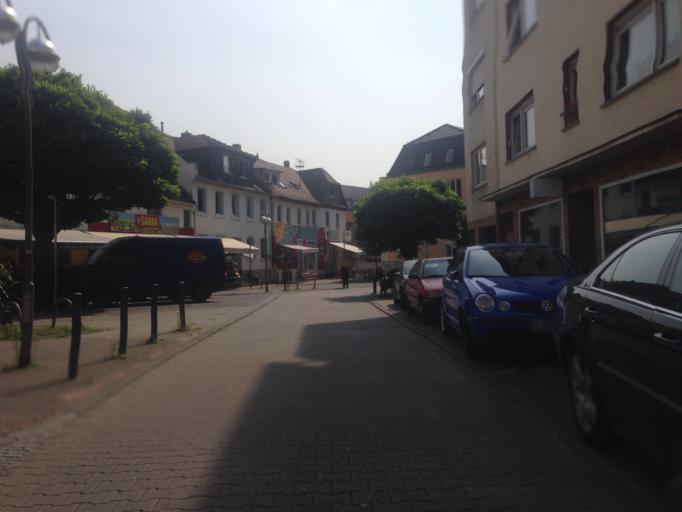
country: DE
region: Hesse
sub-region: Regierungsbezirk Darmstadt
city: Eschborn
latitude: 50.1252
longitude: 8.6124
